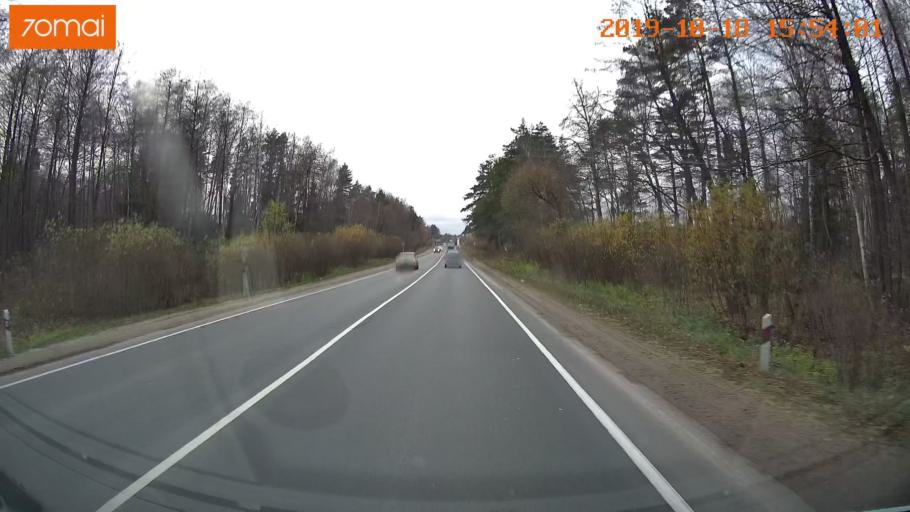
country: RU
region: Vladimir
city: Kommunar
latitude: 56.0601
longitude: 40.5141
